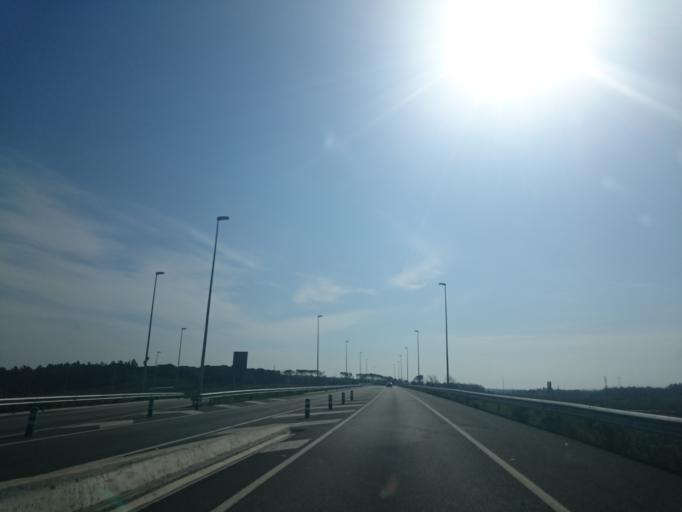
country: ES
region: Catalonia
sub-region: Provincia de Girona
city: Vilobi d'Onyar
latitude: 41.8682
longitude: 2.7750
